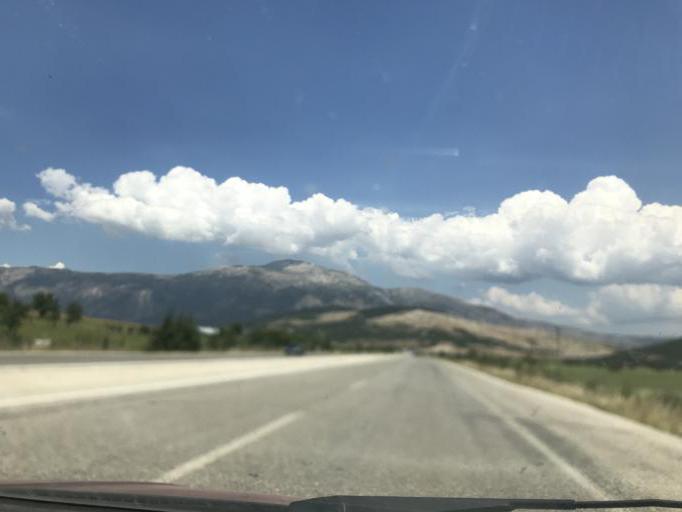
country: TR
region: Denizli
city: Serinhisar
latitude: 37.6220
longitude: 29.1974
